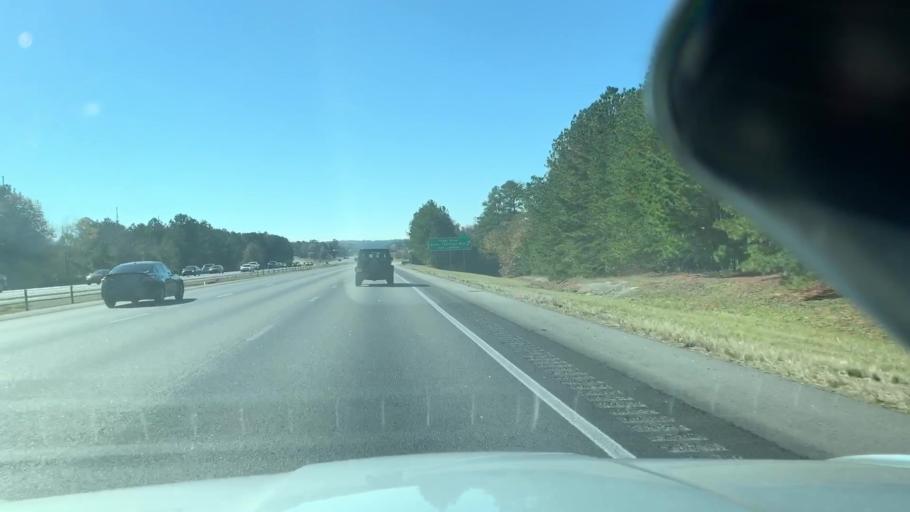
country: US
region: South Carolina
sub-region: Richland County
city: Woodfield
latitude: 34.0280
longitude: -80.9426
